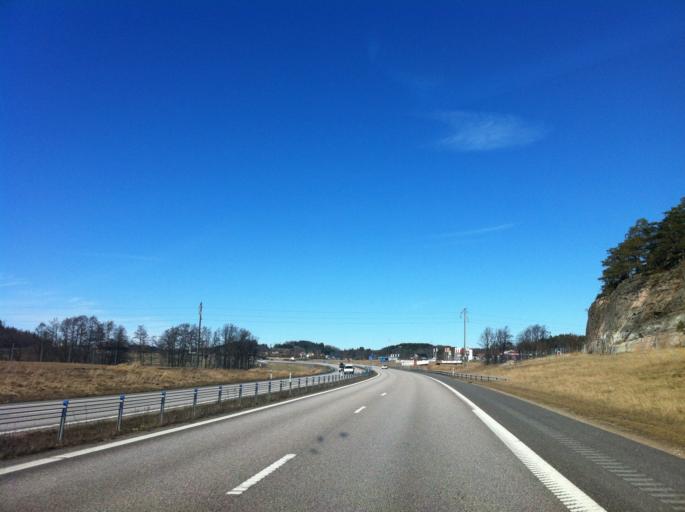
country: SE
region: Vaestra Goetaland
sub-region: Munkedals Kommun
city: Munkedal
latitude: 58.4028
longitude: 11.7420
